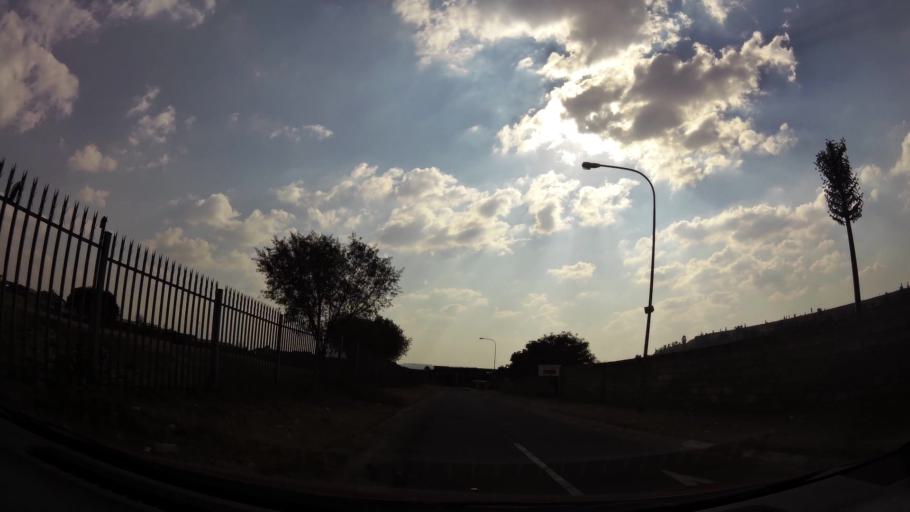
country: ZA
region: Gauteng
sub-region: City of Johannesburg Metropolitan Municipality
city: Johannesburg
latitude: -26.2348
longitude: 27.9514
